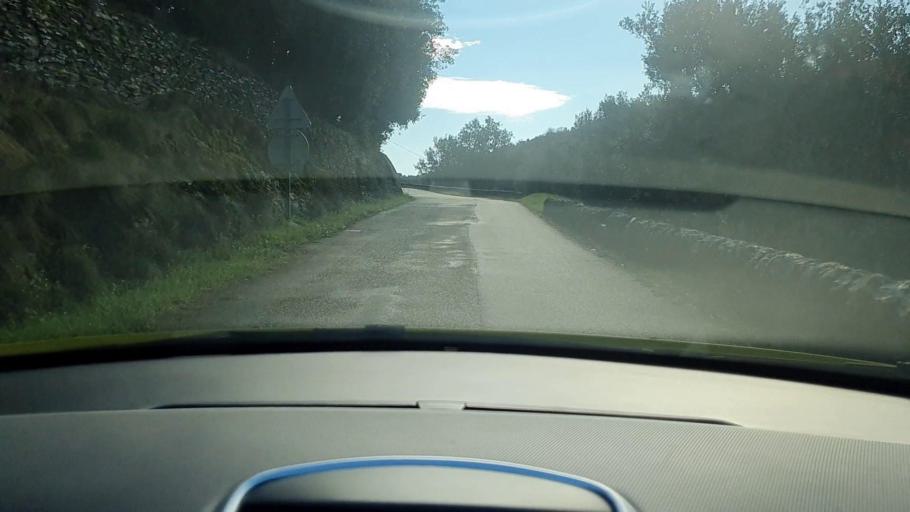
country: FR
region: Languedoc-Roussillon
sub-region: Departement du Gard
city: Valleraugue
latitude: 44.1711
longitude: 3.6475
